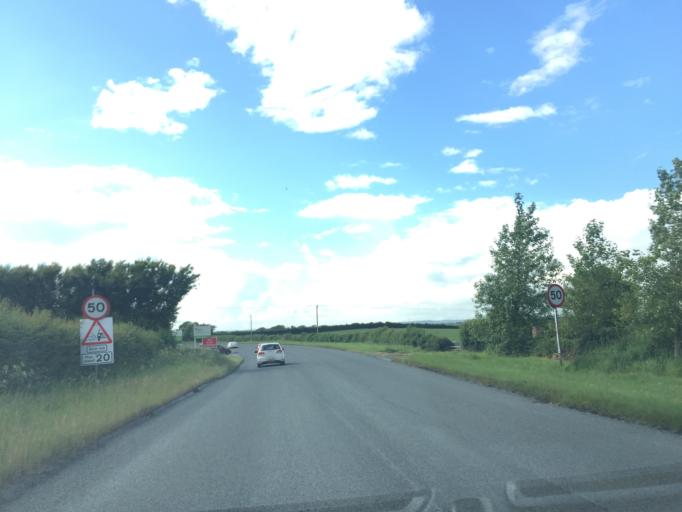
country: GB
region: England
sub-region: Dorset
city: Bovington Camp
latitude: 50.6642
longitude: -2.3190
